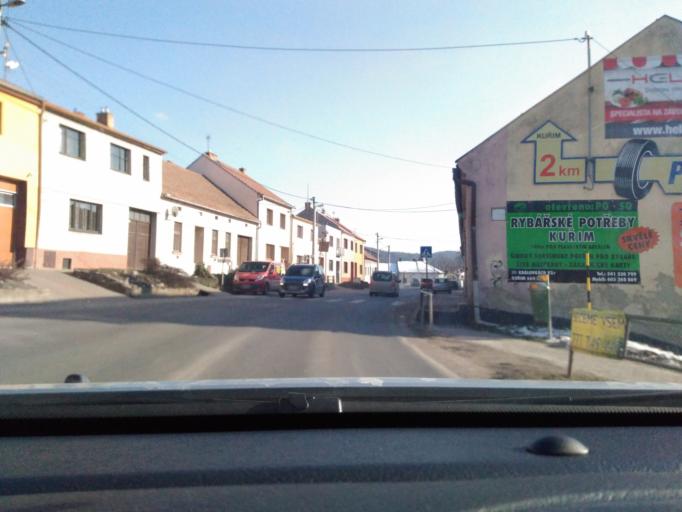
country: CZ
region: South Moravian
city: Cebin
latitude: 49.3160
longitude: 16.4750
